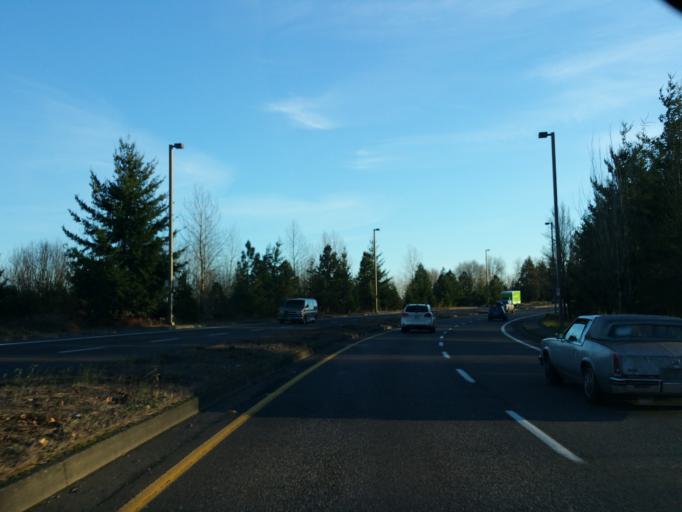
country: US
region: Oregon
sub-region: Multnomah County
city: Fairview
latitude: 45.5520
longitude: -122.4775
